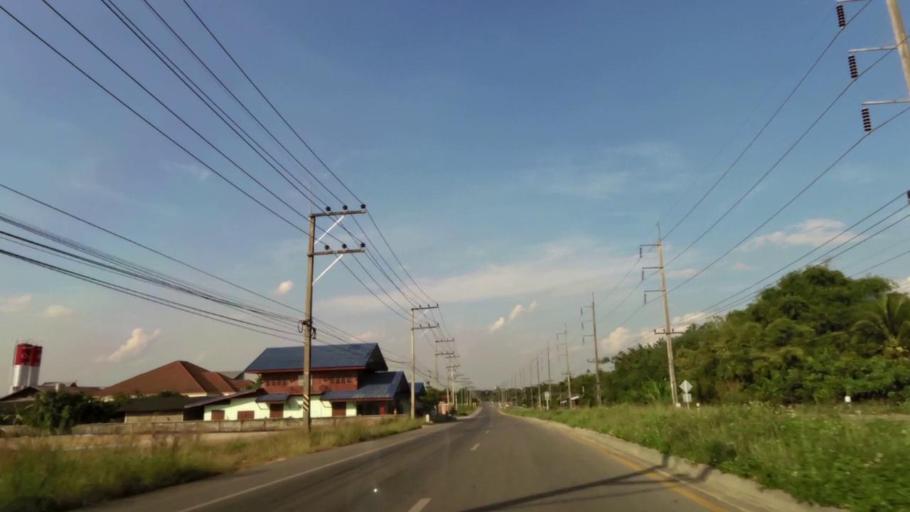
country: TH
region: Chiang Rai
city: Khun Tan
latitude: 19.8999
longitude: 100.2956
